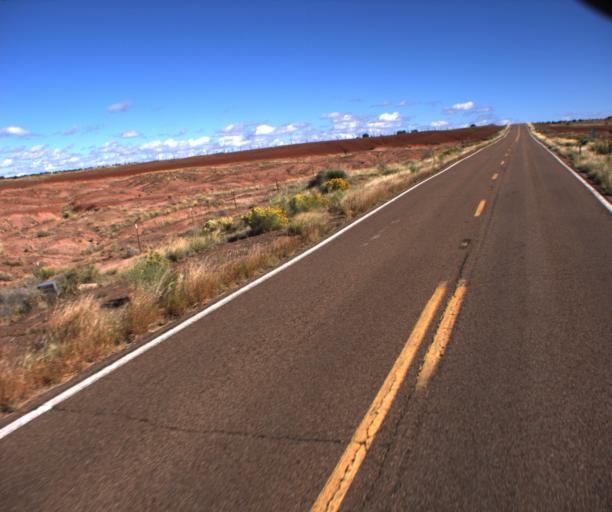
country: US
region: Arizona
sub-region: Apache County
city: Saint Johns
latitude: 34.6428
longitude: -109.3047
